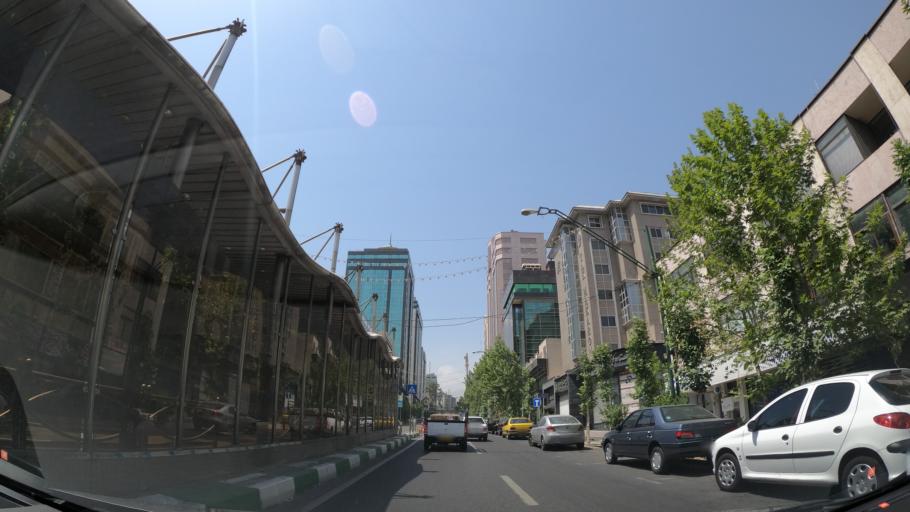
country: IR
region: Tehran
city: Tehran
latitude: 35.7308
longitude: 51.4119
